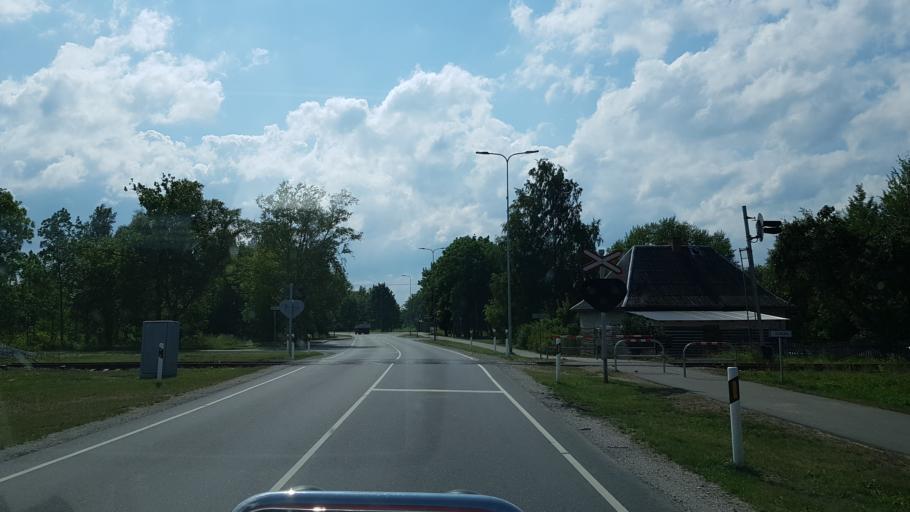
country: EE
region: Ida-Virumaa
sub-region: Kohtla-Jaerve linn
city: Kohtla-Jarve
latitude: 59.3793
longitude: 27.2564
